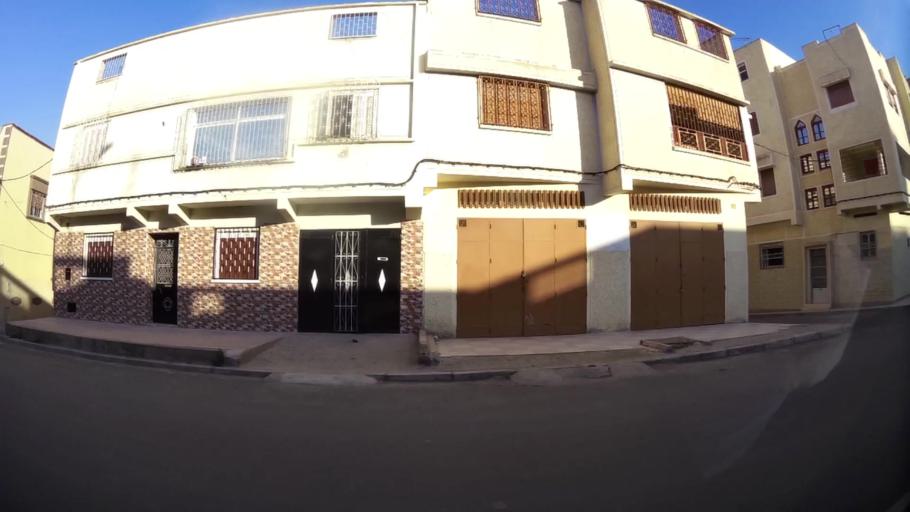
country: MA
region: Oriental
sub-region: Oujda-Angad
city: Oujda
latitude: 34.6980
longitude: -1.9014
